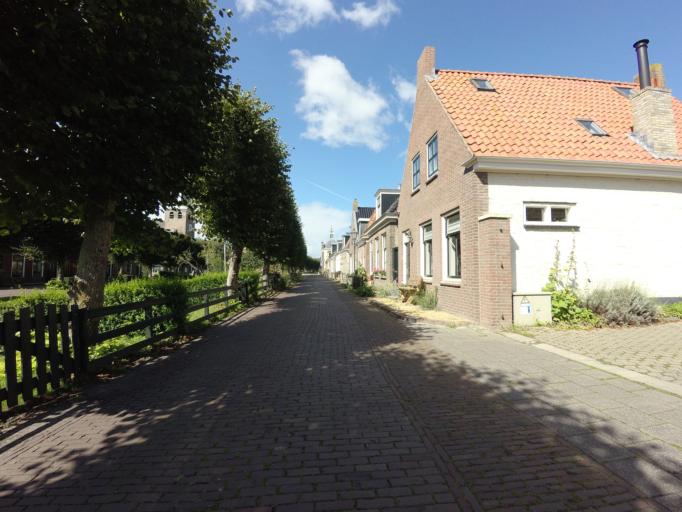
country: NL
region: Friesland
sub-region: Sudwest Fryslan
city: IJlst
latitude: 53.0078
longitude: 5.6250
